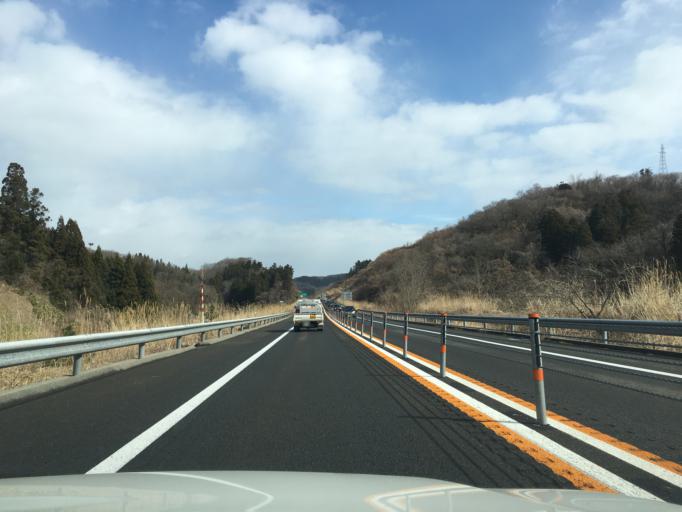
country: JP
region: Akita
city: Akita Shi
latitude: 39.4870
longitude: 140.0549
